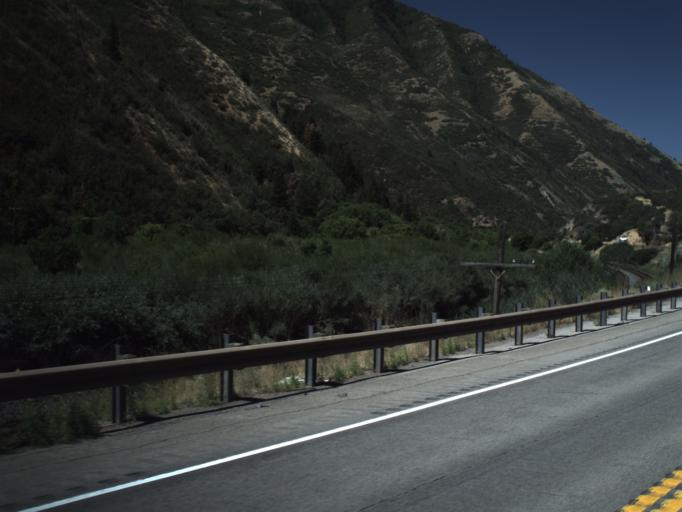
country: US
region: Utah
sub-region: Utah County
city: Mapleton
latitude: 40.0537
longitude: -111.5493
